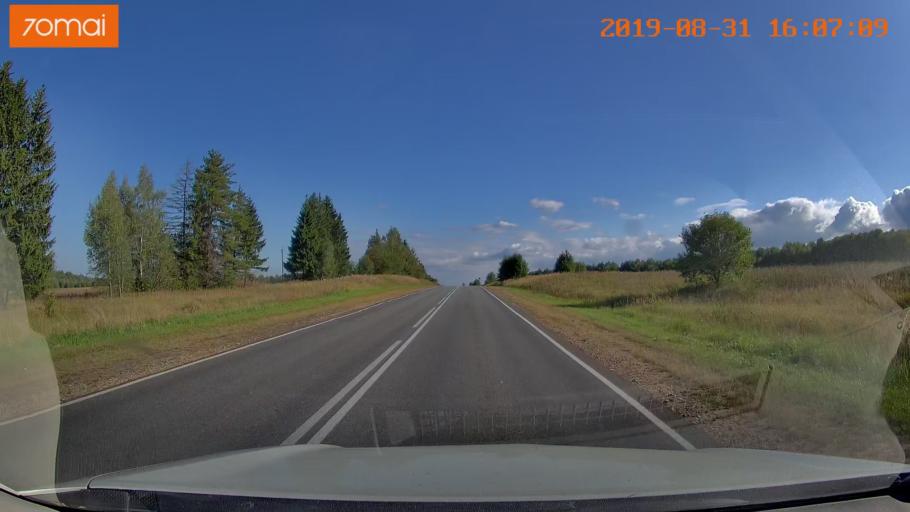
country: RU
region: Kaluga
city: Yukhnov
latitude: 54.6136
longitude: 35.3551
